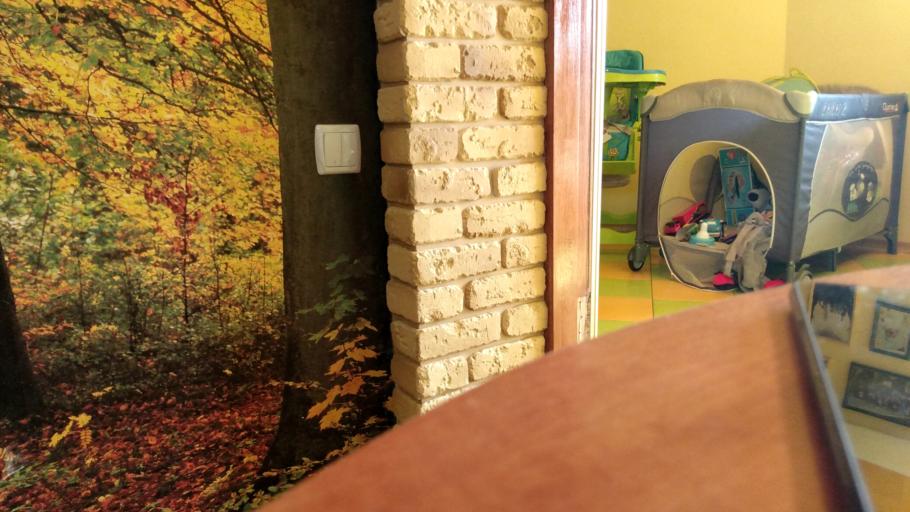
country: RU
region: Tverskaya
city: Sakharovo
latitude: 56.9324
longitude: 36.0014
